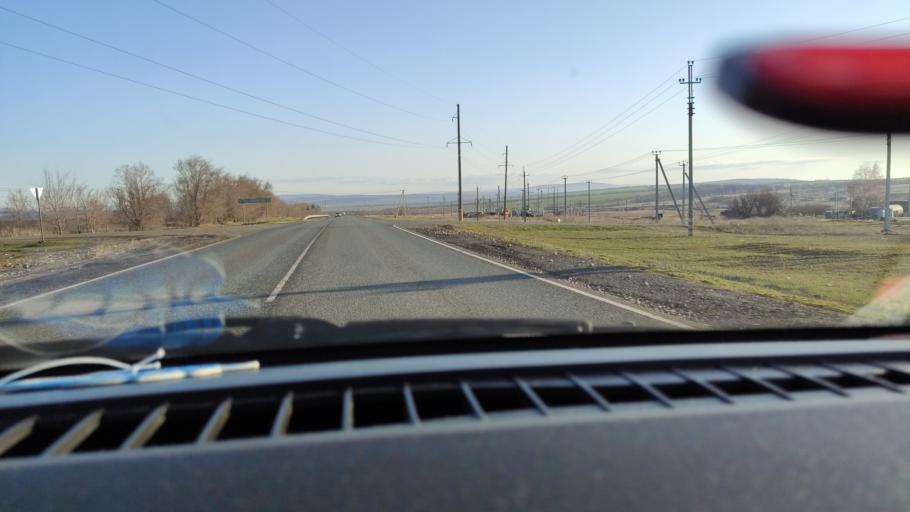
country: RU
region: Saratov
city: Balakovo
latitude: 52.1171
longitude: 47.7514
